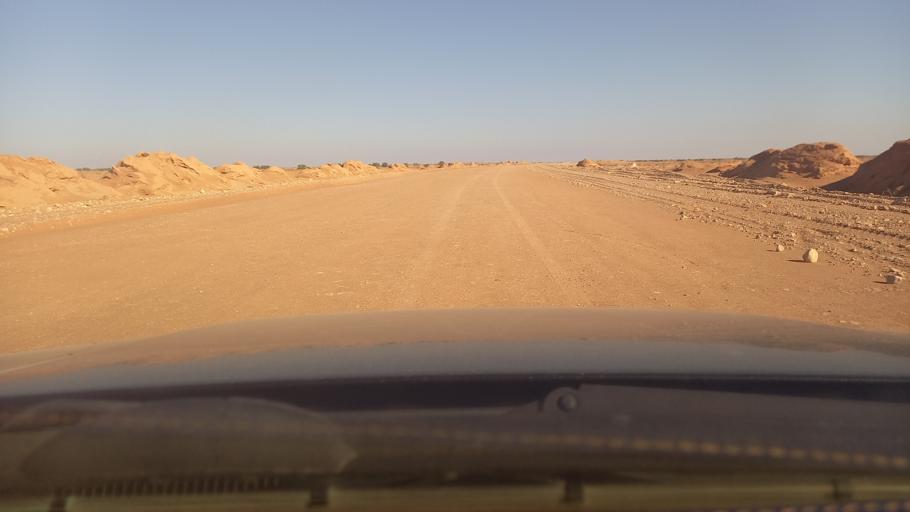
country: TN
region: Madanin
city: Medenine
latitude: 33.1499
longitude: 10.5083
